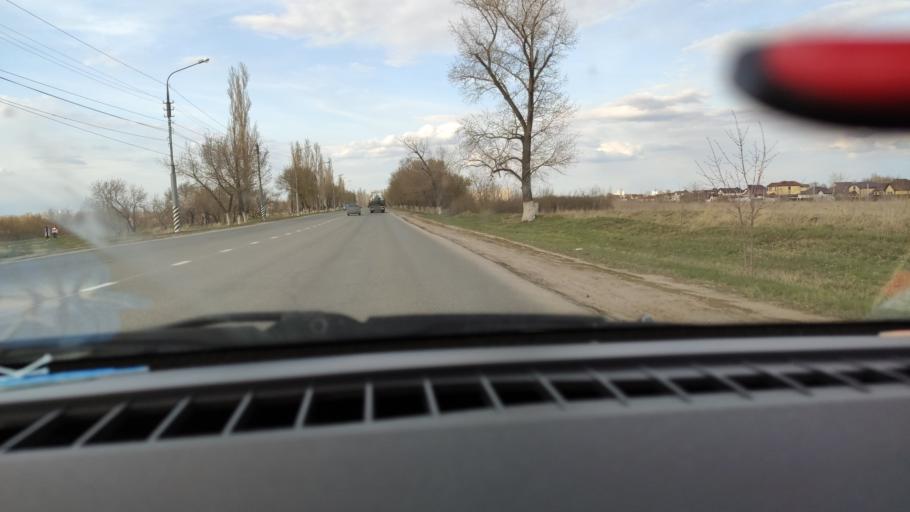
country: RU
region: Saratov
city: Privolzhskiy
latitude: 51.4407
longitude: 46.0675
